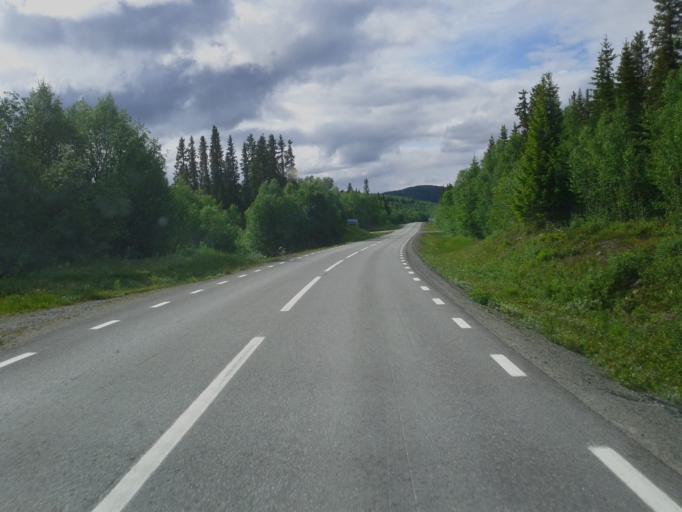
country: NO
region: Nordland
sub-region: Rana
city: Mo i Rana
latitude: 65.7126
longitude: 15.2188
